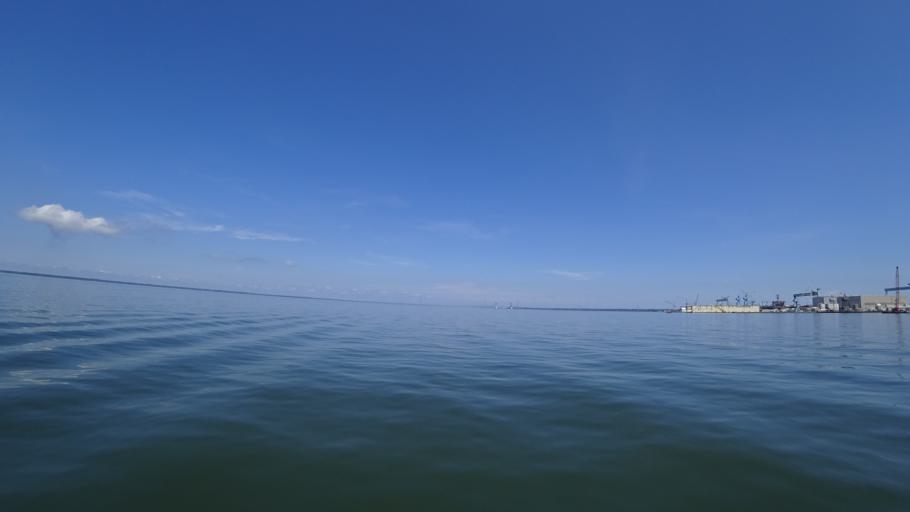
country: US
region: Virginia
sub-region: City of Newport News
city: Newport News
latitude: 36.9790
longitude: -76.4456
